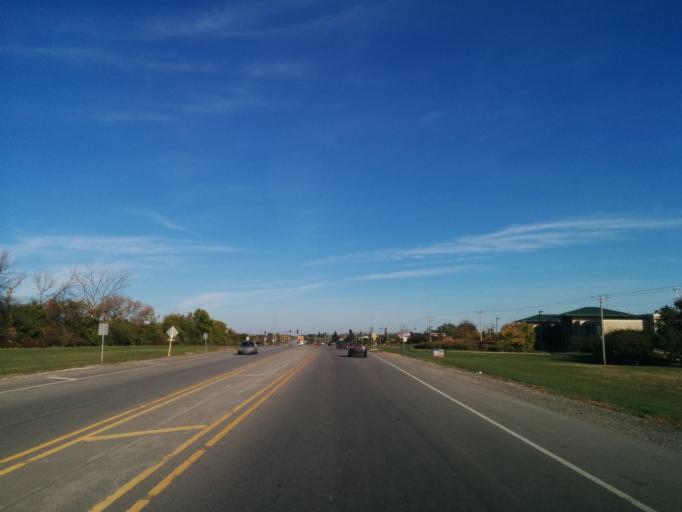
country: US
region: Illinois
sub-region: Kane County
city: North Aurora
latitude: 41.8122
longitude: -88.2877
